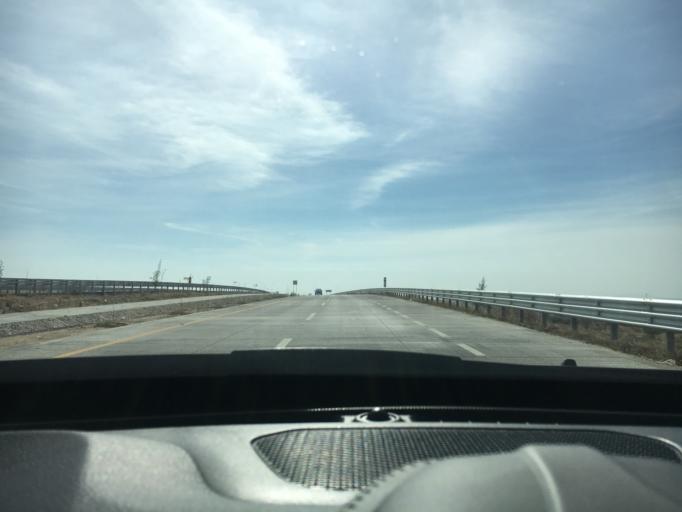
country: MX
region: Guanajuato
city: Duarte
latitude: 21.0524
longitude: -101.5297
